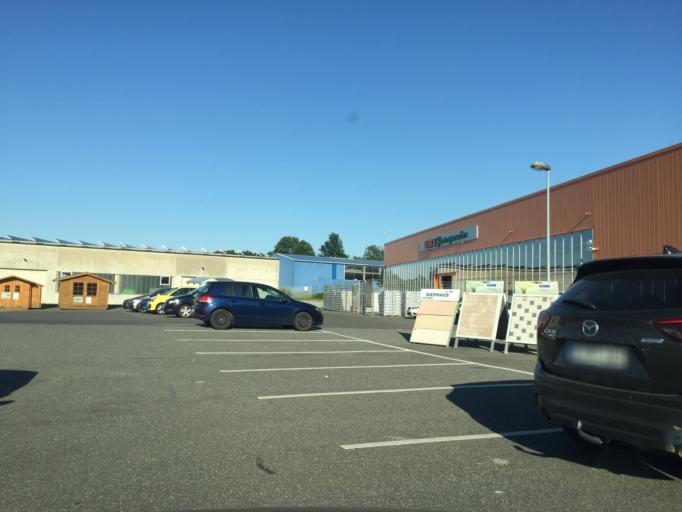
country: DE
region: Bavaria
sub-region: Upper Palatinate
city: Pressath
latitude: 49.7638
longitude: 11.9207
